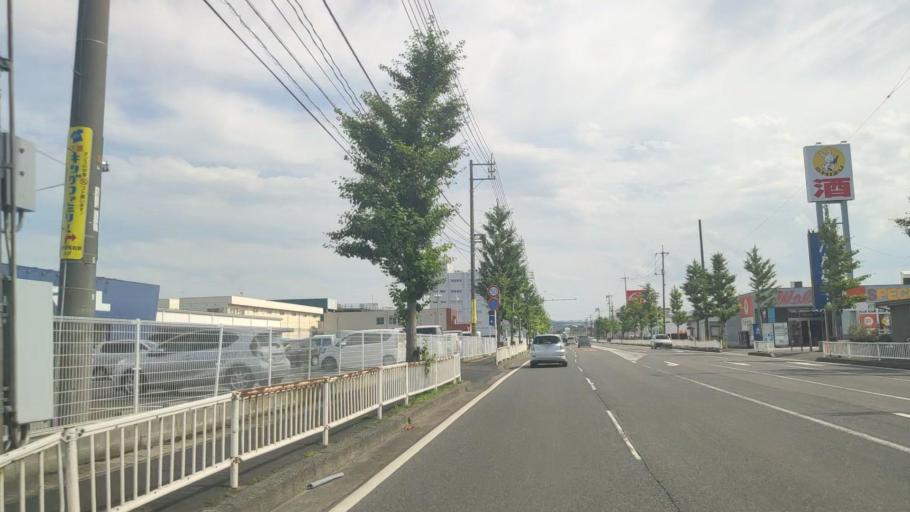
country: JP
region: Tottori
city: Tottori
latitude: 35.5170
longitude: 134.1922
